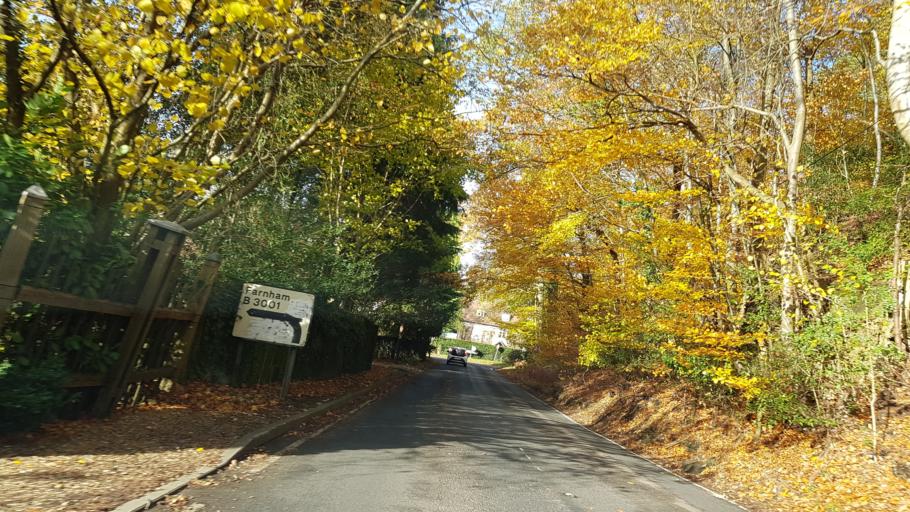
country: GB
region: England
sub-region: Surrey
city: Seale
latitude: 51.2023
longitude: -0.7535
